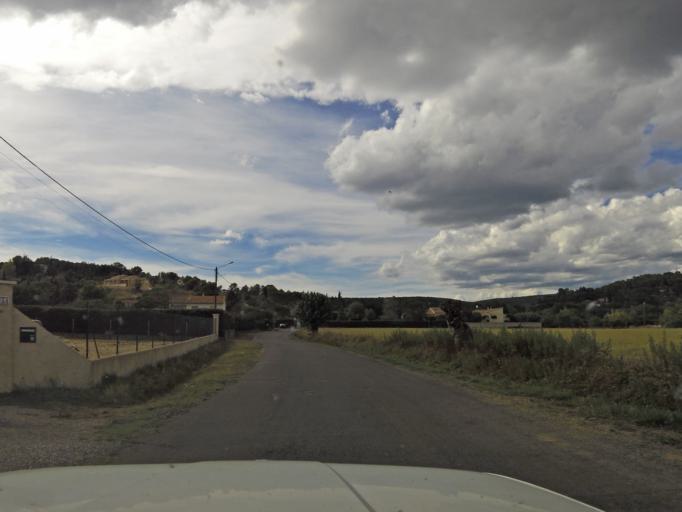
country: FR
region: Languedoc-Roussillon
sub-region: Departement du Gard
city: Saint-Christol-les-Ales
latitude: 44.0869
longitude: 4.0639
